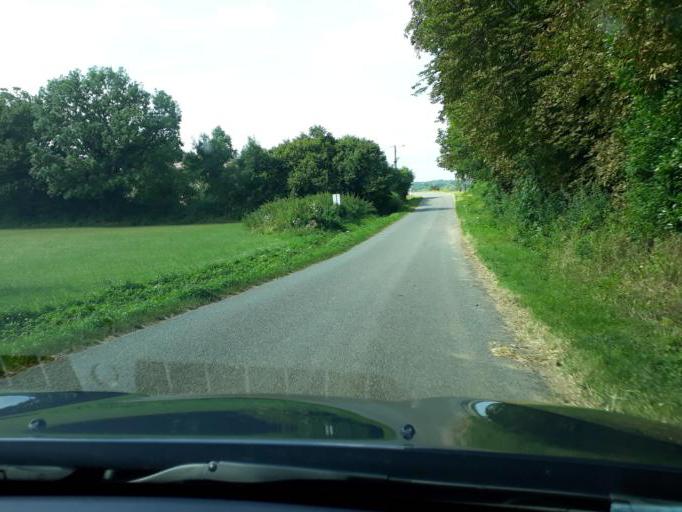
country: FR
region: Centre
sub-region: Departement du Cher
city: Nerondes
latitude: 47.0454
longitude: 2.8885
